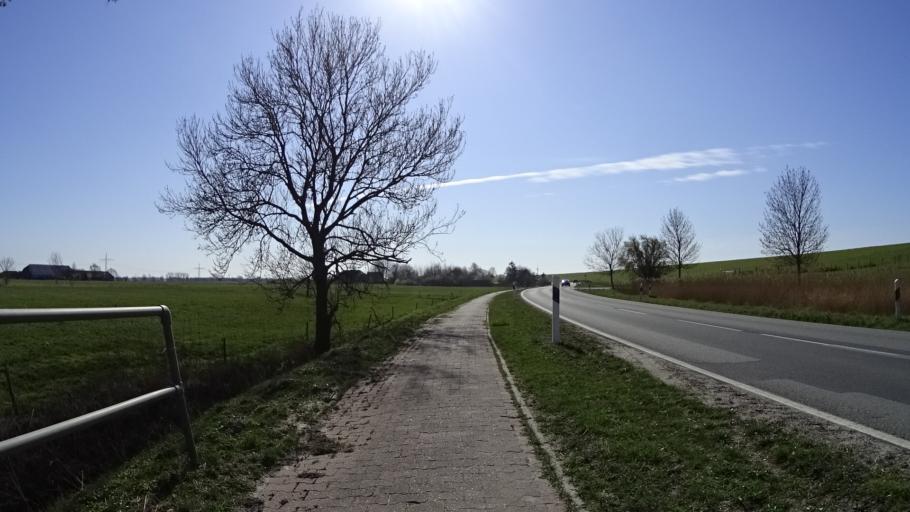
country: DE
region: Lower Saxony
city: Jemgum
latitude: 53.2984
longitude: 7.3906
